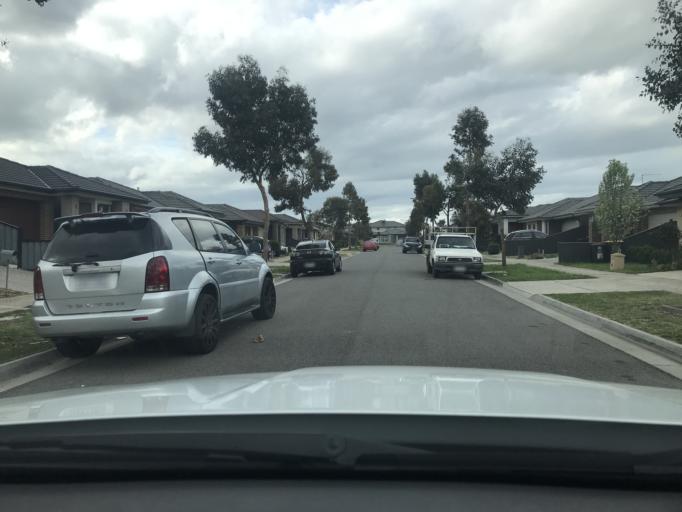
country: AU
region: Victoria
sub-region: Hume
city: Roxburgh Park
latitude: -37.5945
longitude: 144.8974
